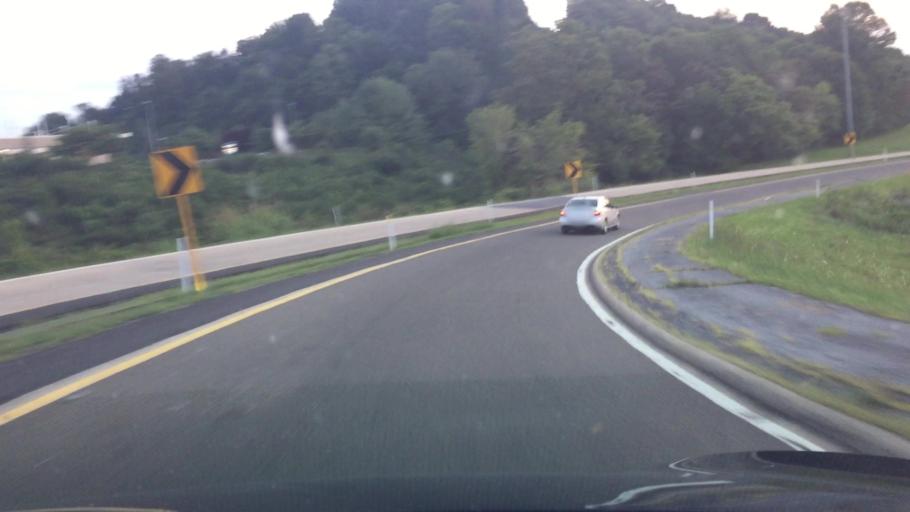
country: US
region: Tennessee
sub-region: Sullivan County
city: Walnut Hill
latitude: 36.5880
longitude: -82.2572
